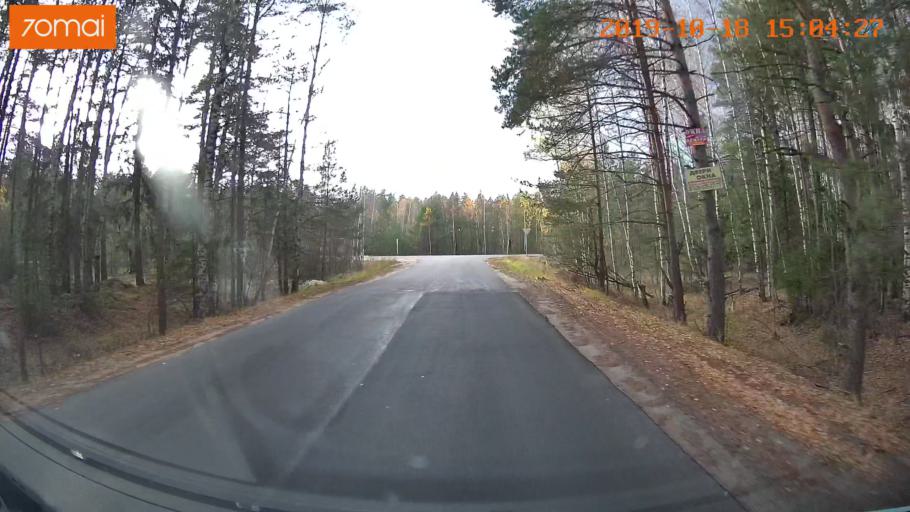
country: RU
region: Vladimir
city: Kurlovo
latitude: 55.5045
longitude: 40.5730
